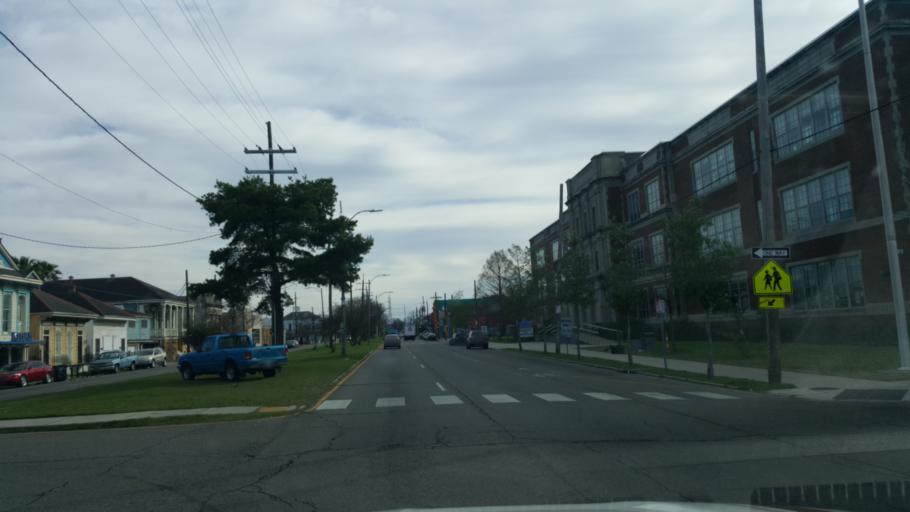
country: US
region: Louisiana
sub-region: Orleans Parish
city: New Orleans
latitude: 29.9687
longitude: -90.0546
